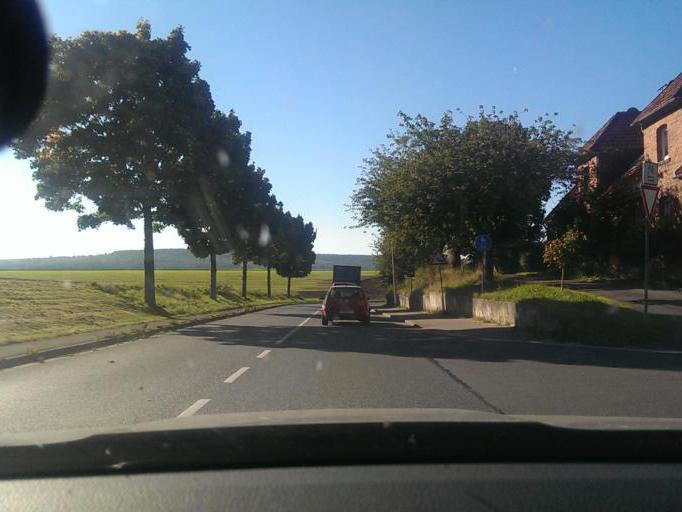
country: DE
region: Lower Saxony
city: Seesen
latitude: 51.9152
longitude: 10.1514
